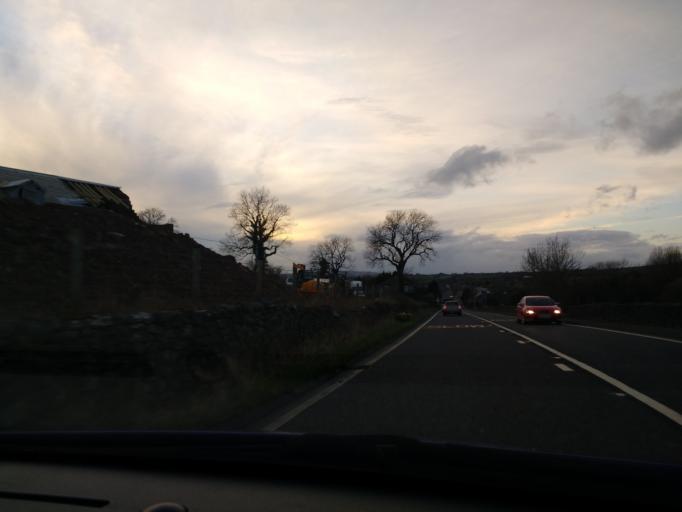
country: GB
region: England
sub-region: North Yorkshire
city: Ingleton
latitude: 54.1446
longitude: -2.4646
